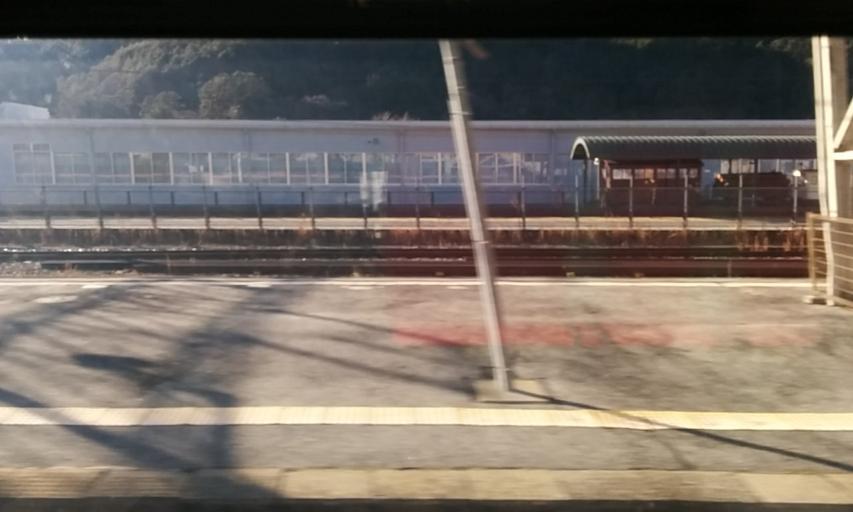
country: JP
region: Nagano
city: Ina
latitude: 35.7837
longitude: 137.6932
